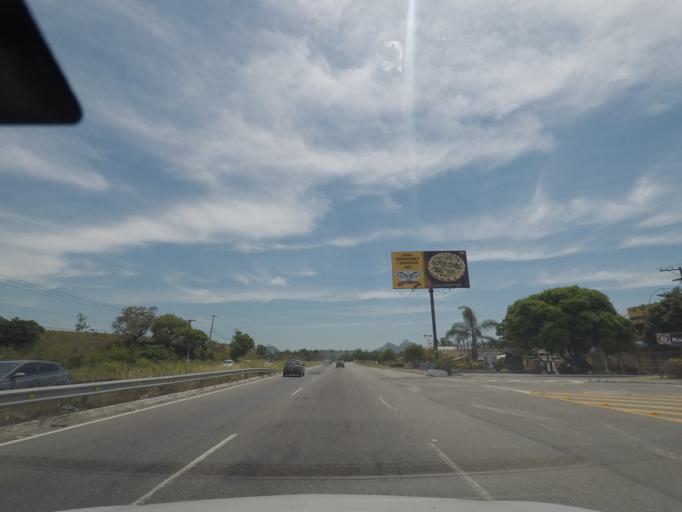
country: BR
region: Rio de Janeiro
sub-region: Marica
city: Marica
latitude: -22.9158
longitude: -42.8490
